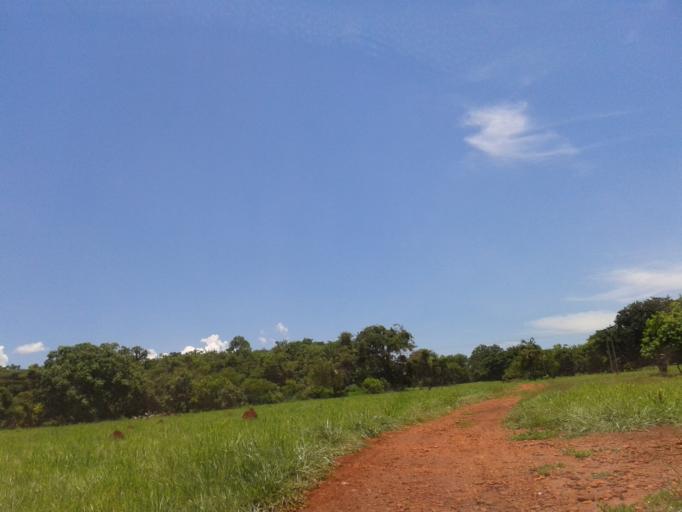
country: BR
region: Minas Gerais
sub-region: Santa Vitoria
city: Santa Vitoria
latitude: -19.1254
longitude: -50.5628
